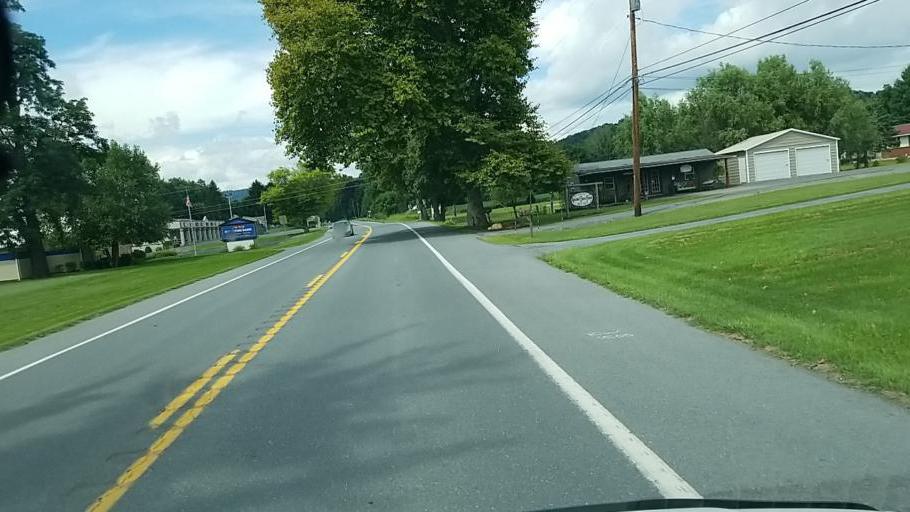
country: US
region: Pennsylvania
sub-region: Dauphin County
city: Matamoras
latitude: 40.4899
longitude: -76.9344
